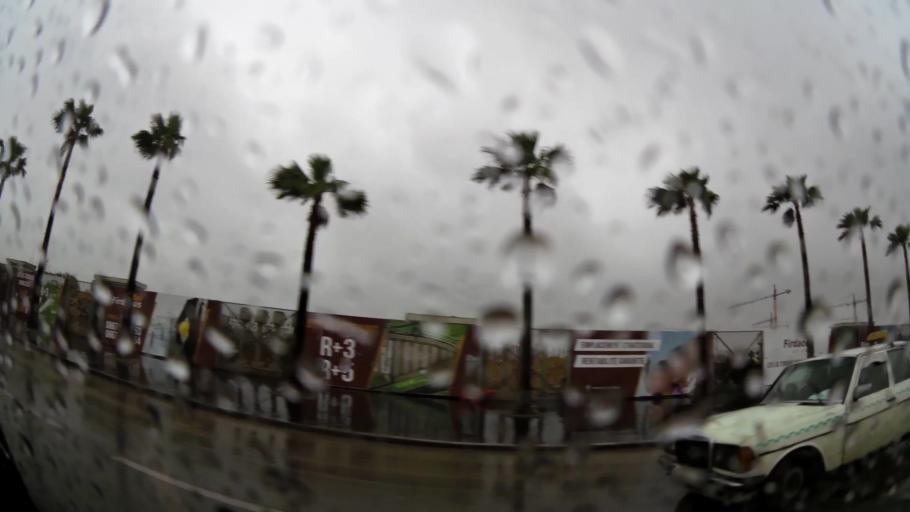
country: MA
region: Grand Casablanca
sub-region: Mediouna
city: Tit Mellil
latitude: 33.6017
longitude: -7.5121
